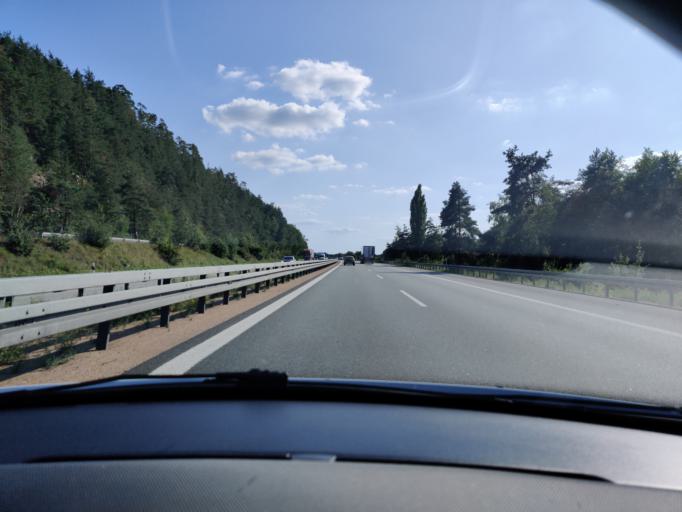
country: DE
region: Bavaria
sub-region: Upper Palatinate
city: Nabburg
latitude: 49.4235
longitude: 12.1701
